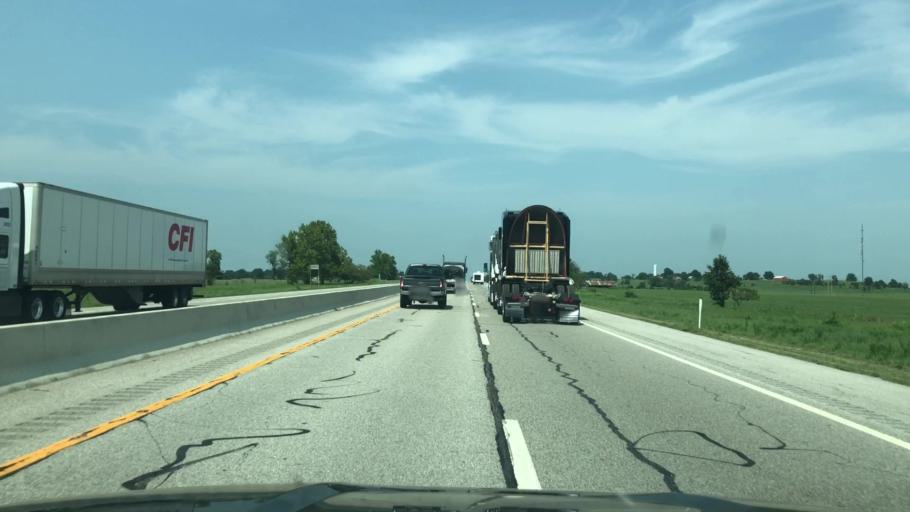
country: US
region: Oklahoma
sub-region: Ottawa County
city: Miami
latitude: 36.8186
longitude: -94.8720
